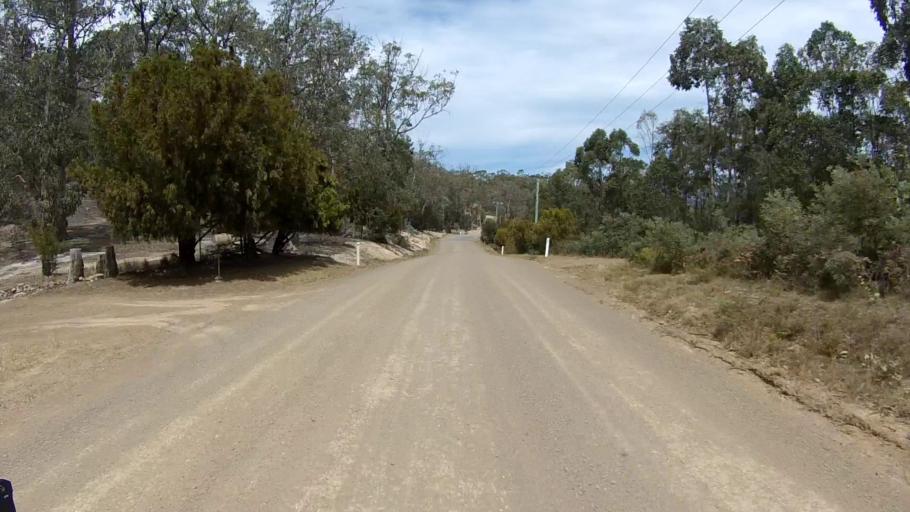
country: AU
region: Tasmania
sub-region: Sorell
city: Sorell
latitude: -42.7991
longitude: 147.6820
